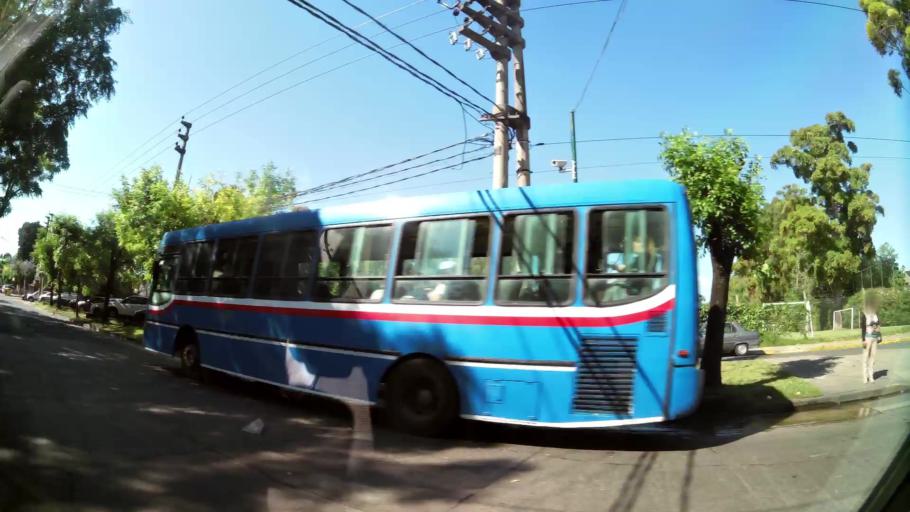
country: AR
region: Buenos Aires
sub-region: Partido de Tigre
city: Tigre
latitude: -34.4779
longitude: -58.5722
